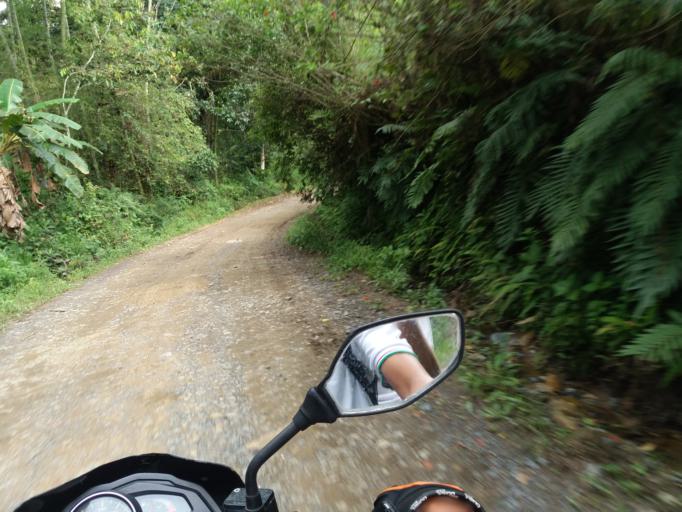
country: CO
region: Santander
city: Guepsa
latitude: 6.0055
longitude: -73.5452
